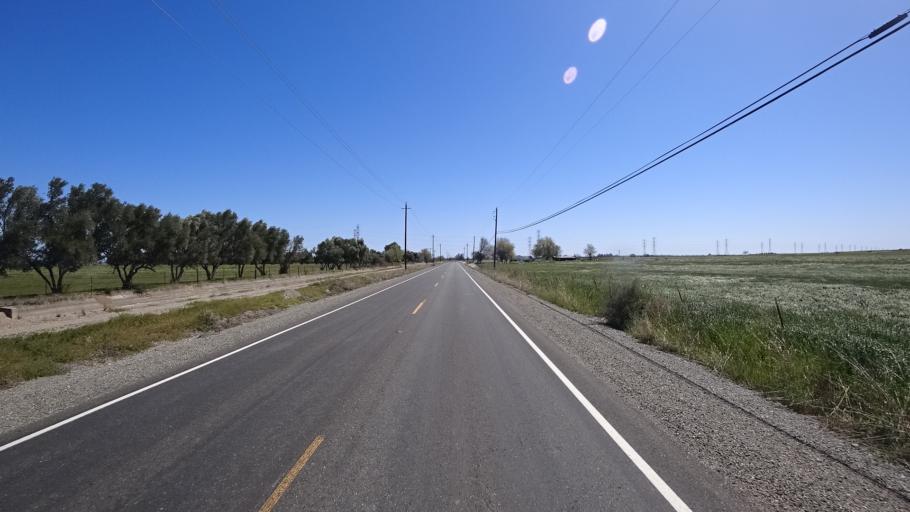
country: US
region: California
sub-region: Glenn County
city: Orland
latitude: 39.7740
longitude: -122.2695
